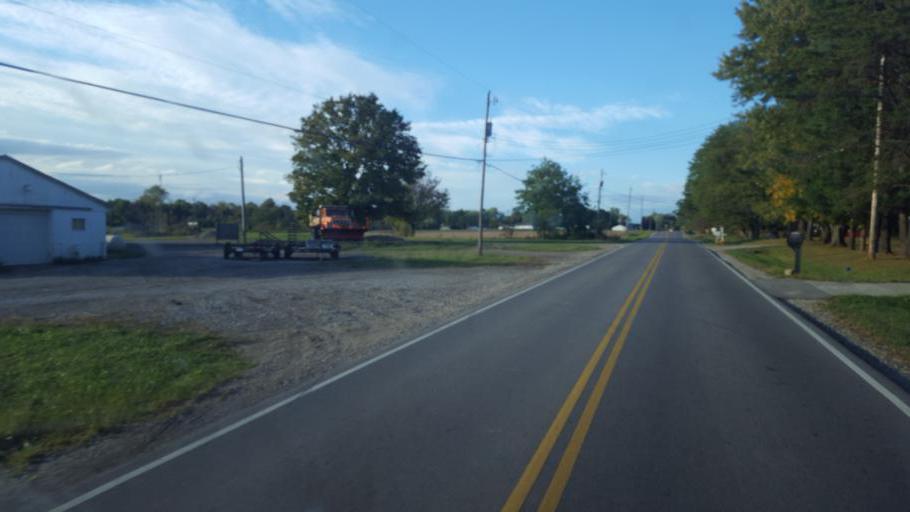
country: US
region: Ohio
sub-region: Licking County
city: Pataskala
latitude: 40.0280
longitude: -82.7317
